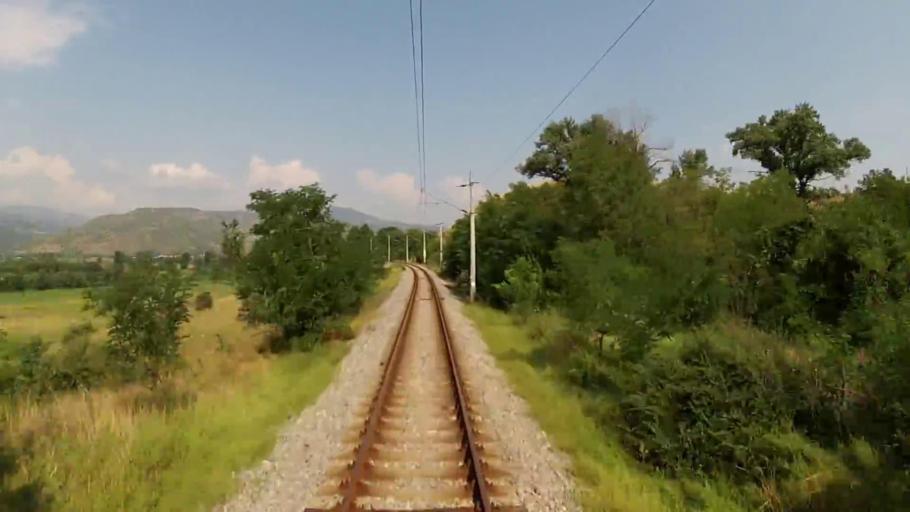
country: BG
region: Blagoevgrad
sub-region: Obshtina Sandanski
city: Sandanski
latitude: 41.5264
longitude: 23.2656
